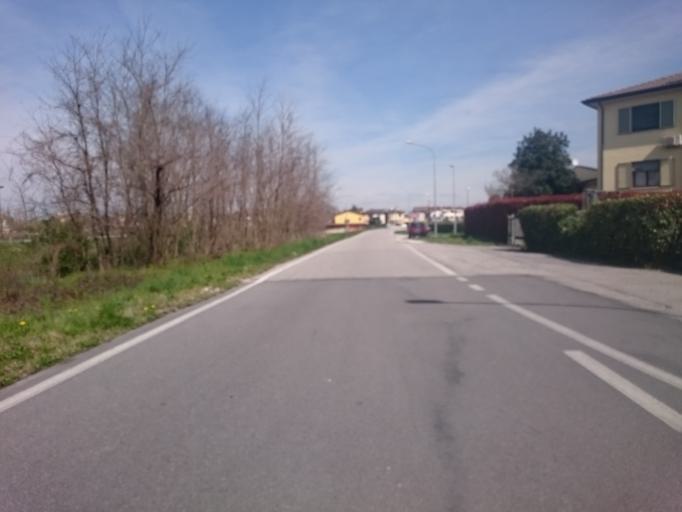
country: IT
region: Veneto
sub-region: Provincia di Padova
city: Limena
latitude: 45.4769
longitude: 11.8405
